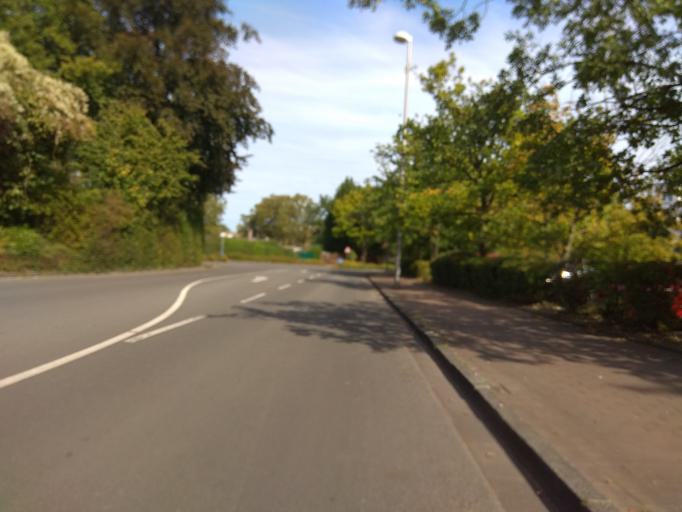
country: DE
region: North Rhine-Westphalia
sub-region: Regierungsbezirk Munster
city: Klein Reken
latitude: 51.7263
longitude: 7.0386
